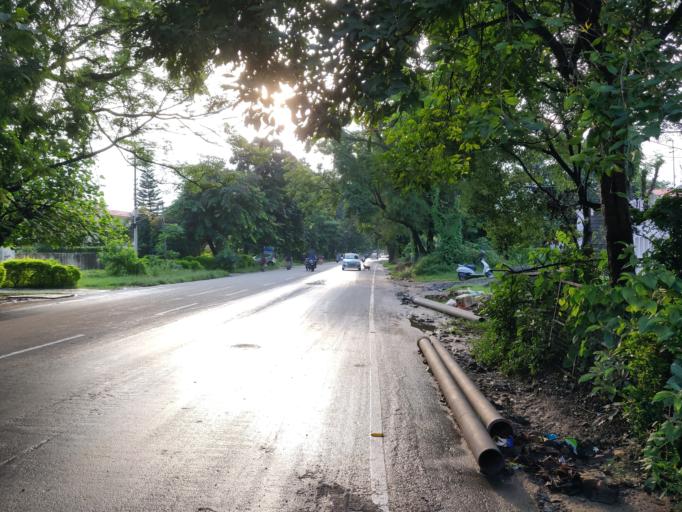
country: IN
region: Uttarakhand
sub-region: Dehradun
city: Dehradun
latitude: 30.3260
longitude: 78.0006
